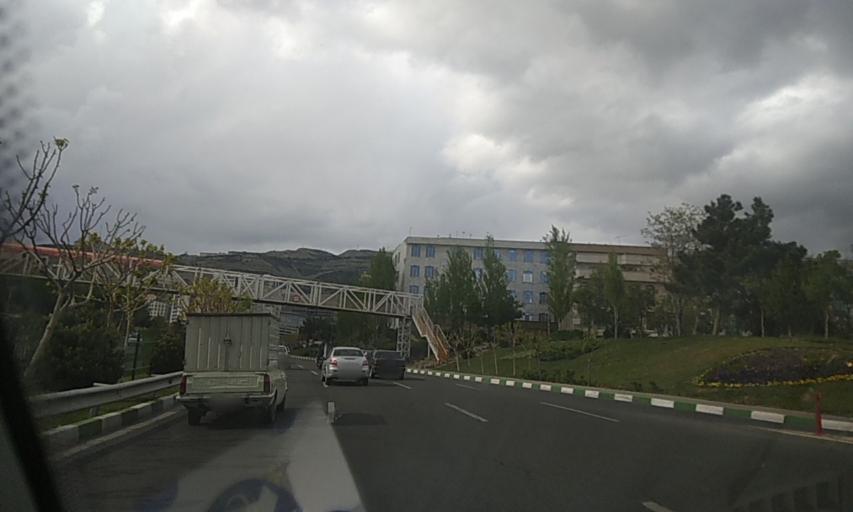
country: IR
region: Tehran
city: Tajrish
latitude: 35.7740
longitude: 51.3208
